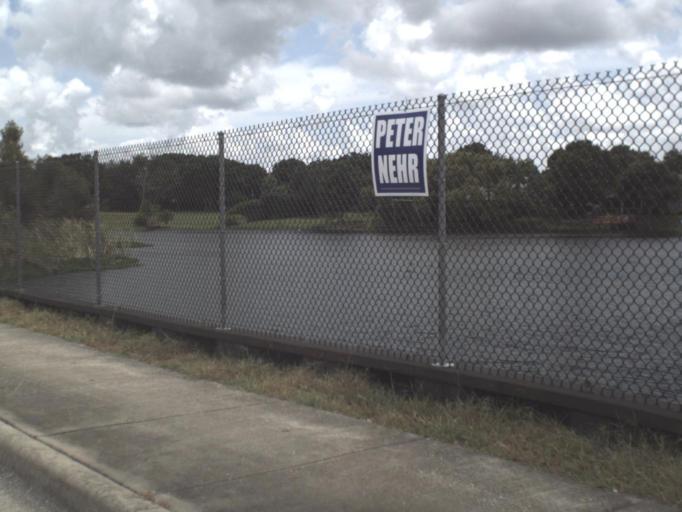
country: US
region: Florida
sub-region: Pinellas County
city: Saint George
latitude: 28.0499
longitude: -82.7293
